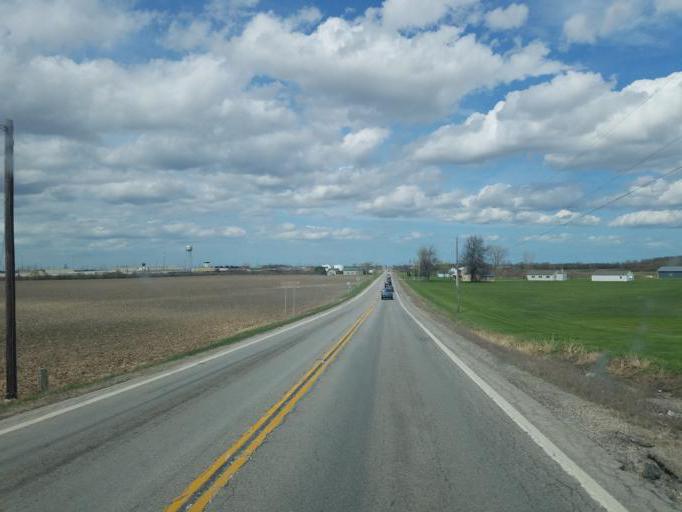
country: US
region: Ohio
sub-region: Huron County
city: Bellevue
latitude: 41.2842
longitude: -82.7860
